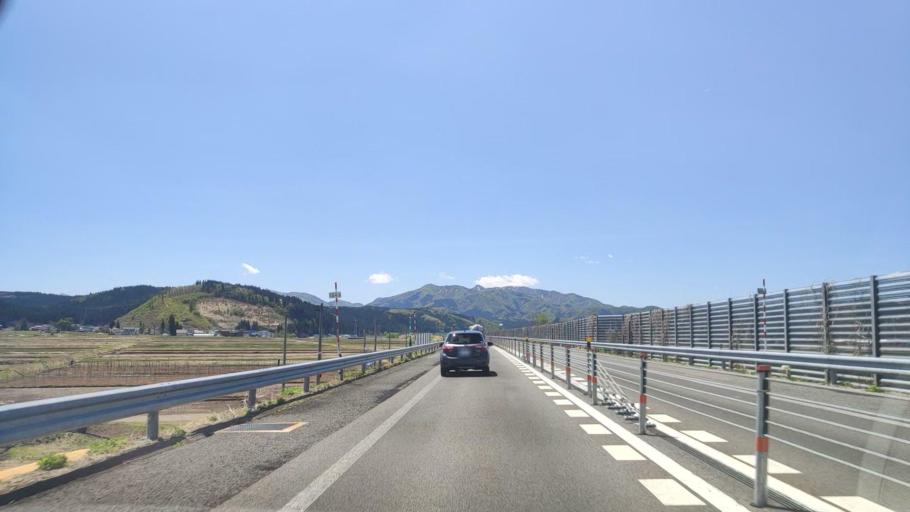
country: JP
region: Akita
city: Yuzawa
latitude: 39.0771
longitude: 140.4757
